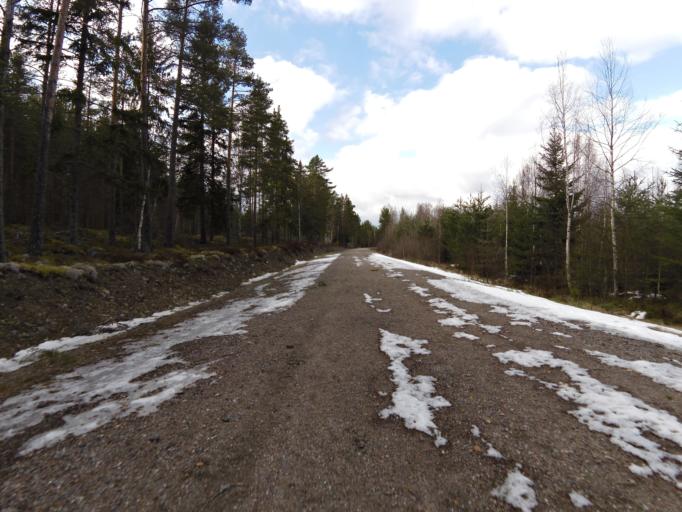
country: SE
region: Gaevleborg
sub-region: Hofors Kommun
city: Hofors
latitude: 60.4802
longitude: 16.4484
